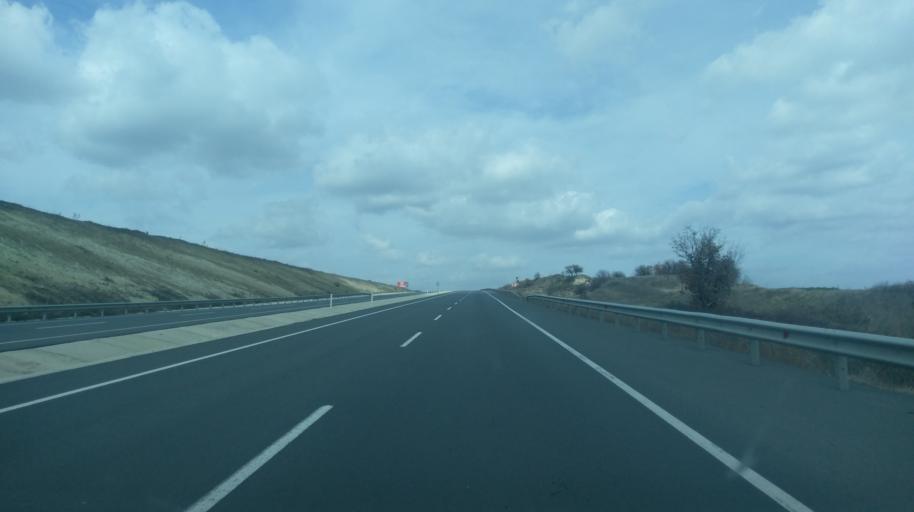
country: TR
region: Edirne
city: Kesan
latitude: 40.9349
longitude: 26.6366
